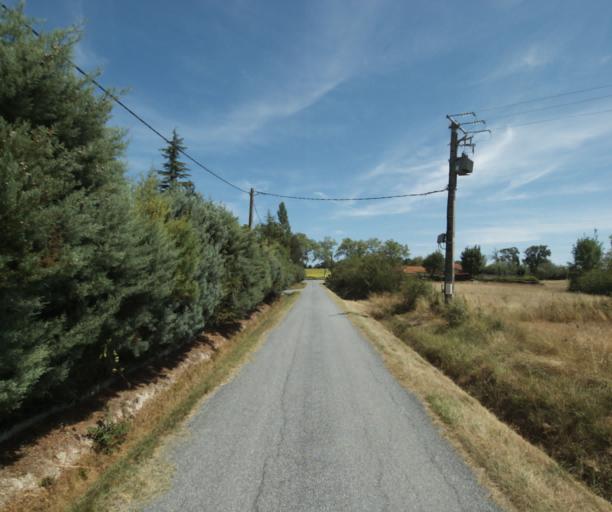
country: FR
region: Midi-Pyrenees
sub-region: Departement de la Haute-Garonne
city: Revel
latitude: 43.5059
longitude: 2.0099
